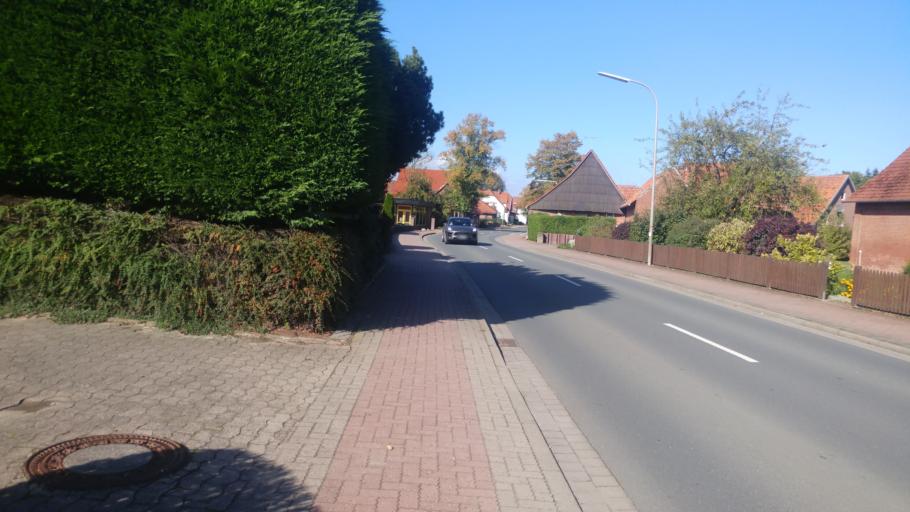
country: DE
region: Lower Saxony
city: Lauenhagen
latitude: 52.3576
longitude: 9.2076
